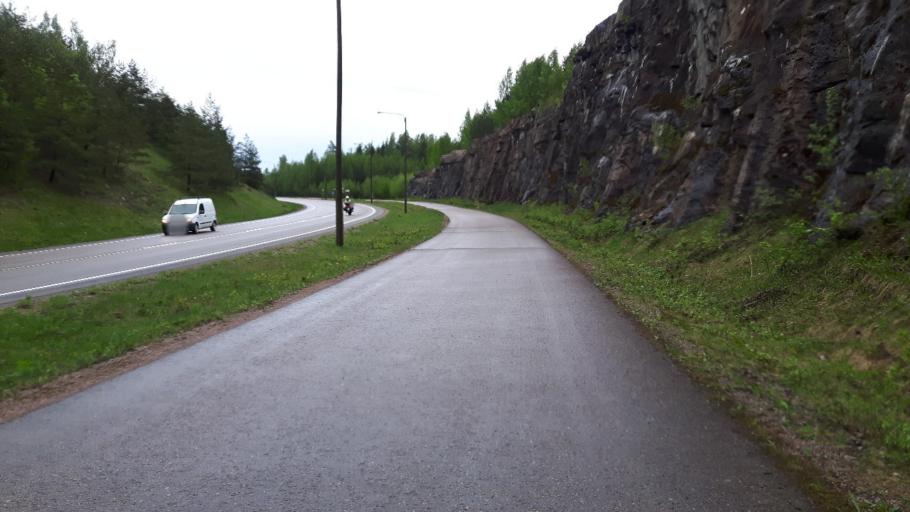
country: FI
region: Kymenlaakso
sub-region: Kotka-Hamina
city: Karhula
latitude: 60.5595
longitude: 27.0161
